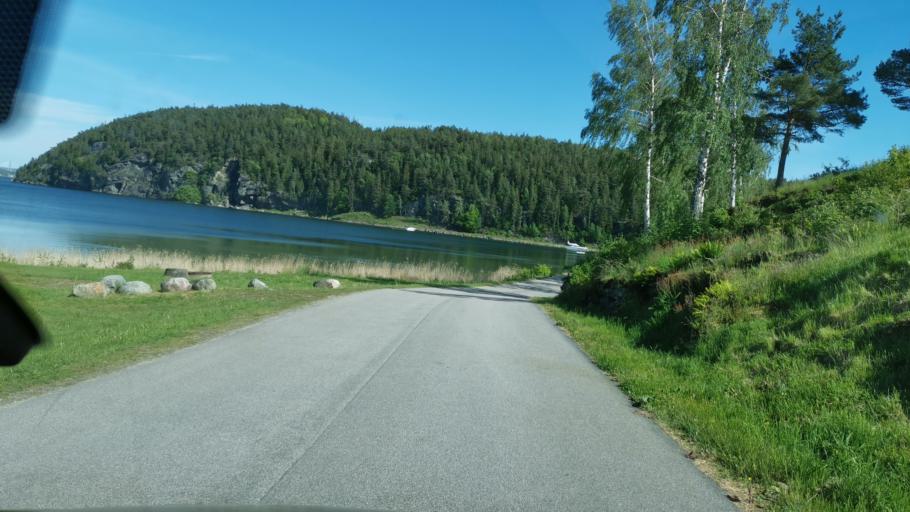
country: SE
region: Vaestra Goetaland
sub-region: Orust
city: Henan
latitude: 58.3173
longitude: 11.7213
